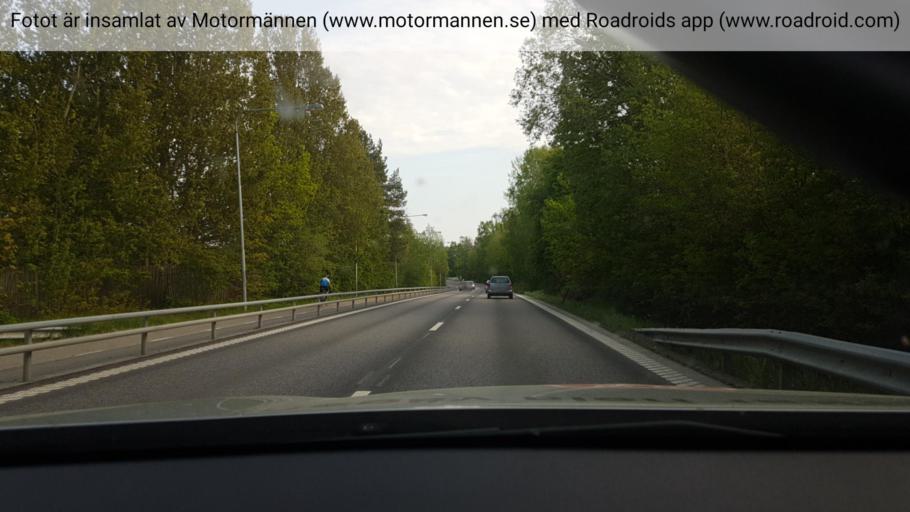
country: SE
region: Stockholm
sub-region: Tyreso Kommun
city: Bollmora
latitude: 59.2202
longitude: 18.2030
